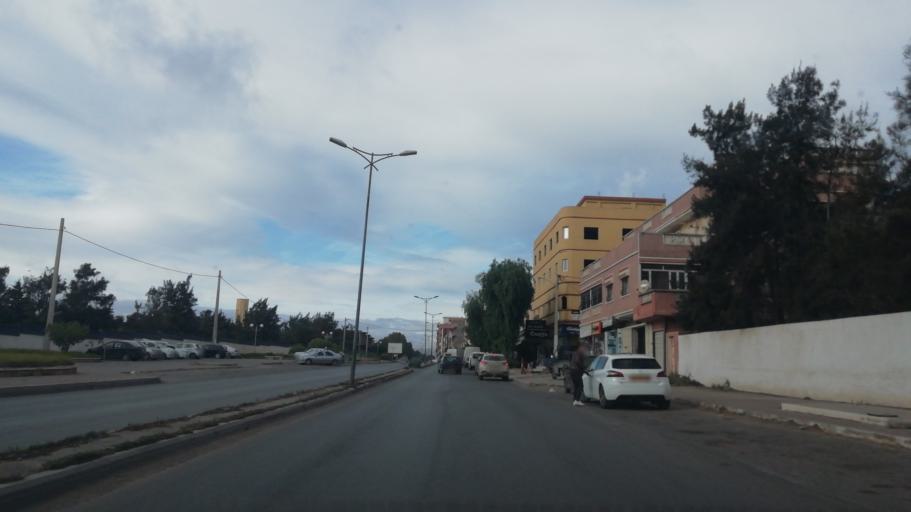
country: DZ
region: Oran
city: Bir el Djir
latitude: 35.7130
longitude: -0.5839
